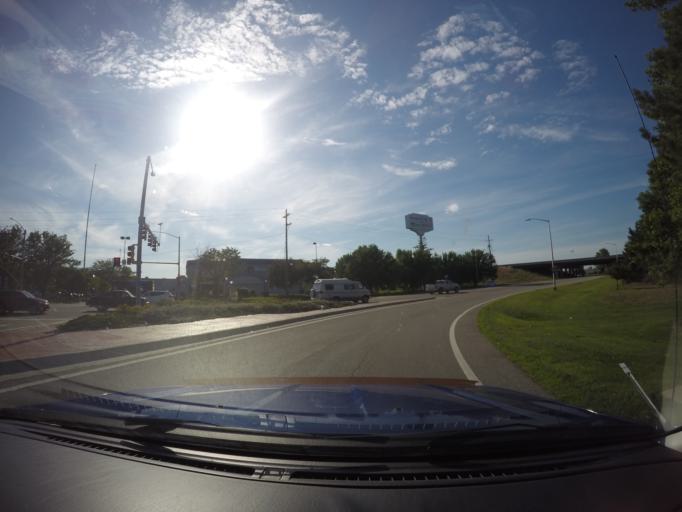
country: US
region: Kansas
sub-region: Douglas County
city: Lawrence
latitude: 38.9916
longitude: -95.2330
